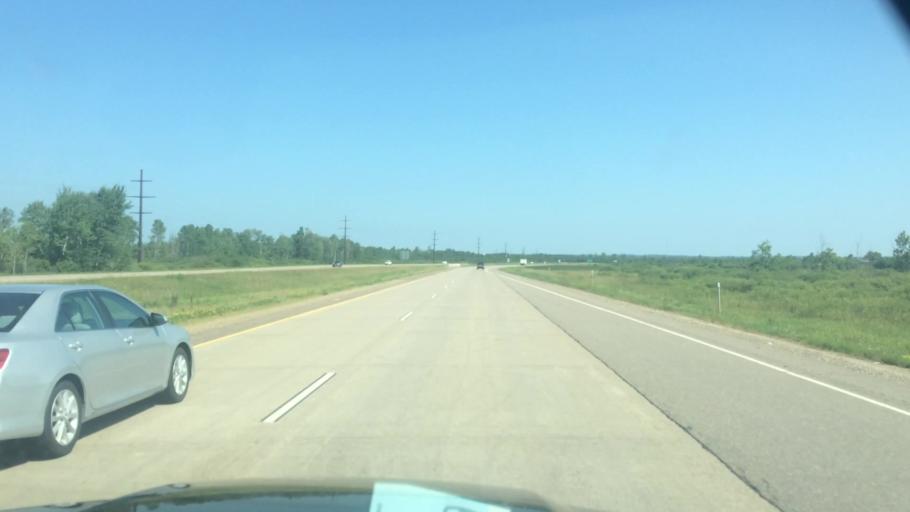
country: US
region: Wisconsin
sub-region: Lincoln County
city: Merrill
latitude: 45.2164
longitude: -89.6697
